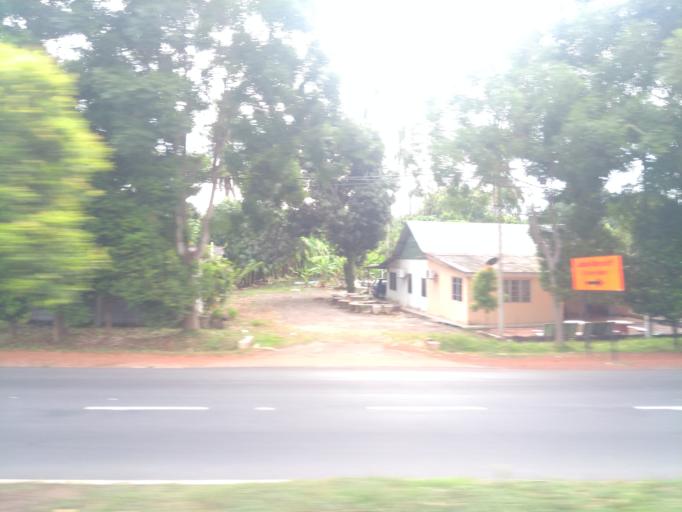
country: MY
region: Melaka
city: Kampung Ayer Keroh
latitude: 2.2822
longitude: 102.2625
